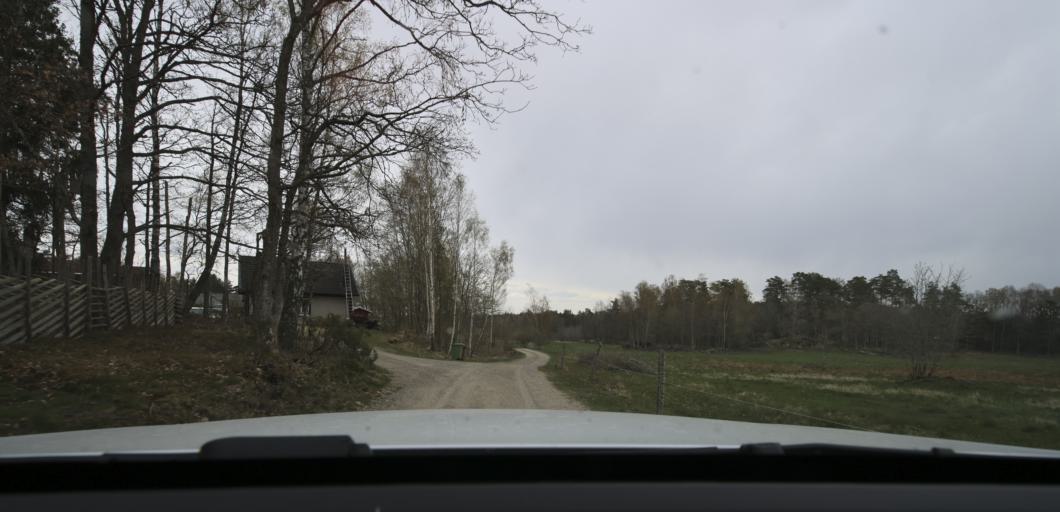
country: SE
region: Halland
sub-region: Varbergs Kommun
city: Tvaaker
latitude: 57.1247
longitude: 12.4585
